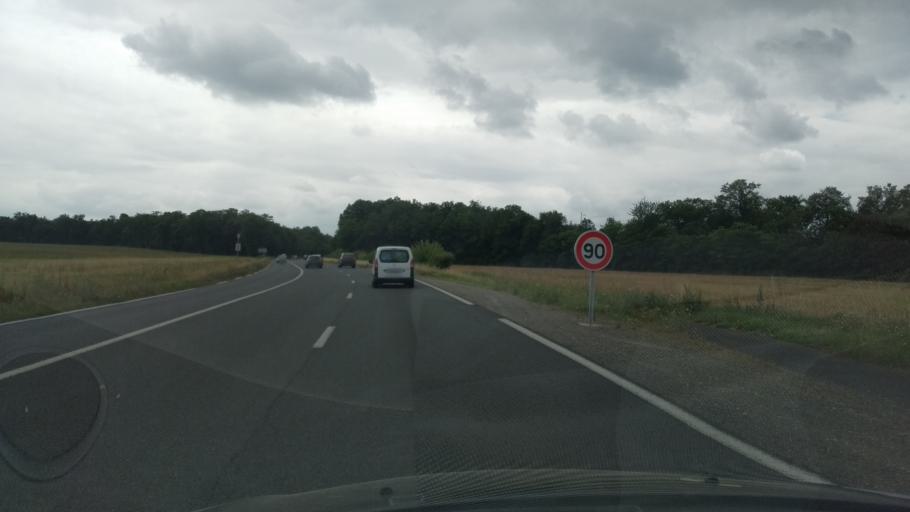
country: FR
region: Poitou-Charentes
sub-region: Departement de la Vienne
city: Saint-Benoit
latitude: 46.5396
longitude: 0.3548
